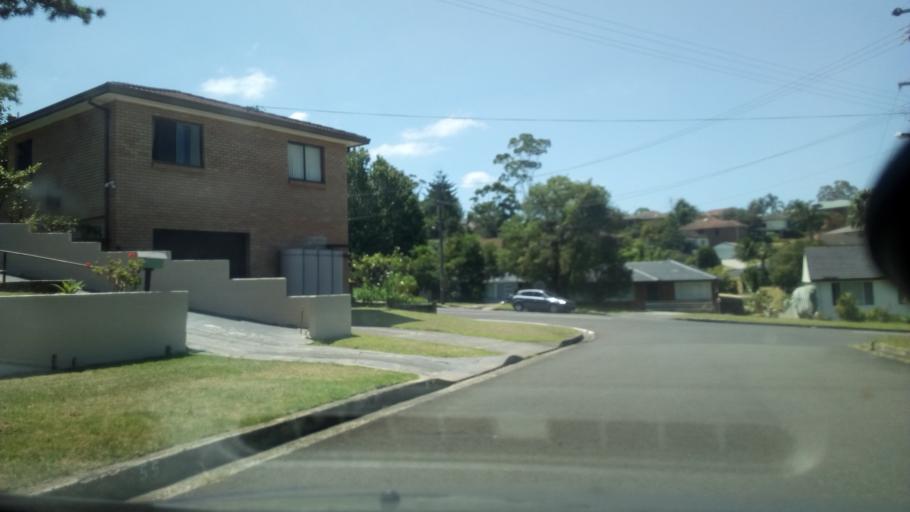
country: AU
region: New South Wales
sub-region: Wollongong
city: West Wollongong
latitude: -34.4271
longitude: 150.8566
